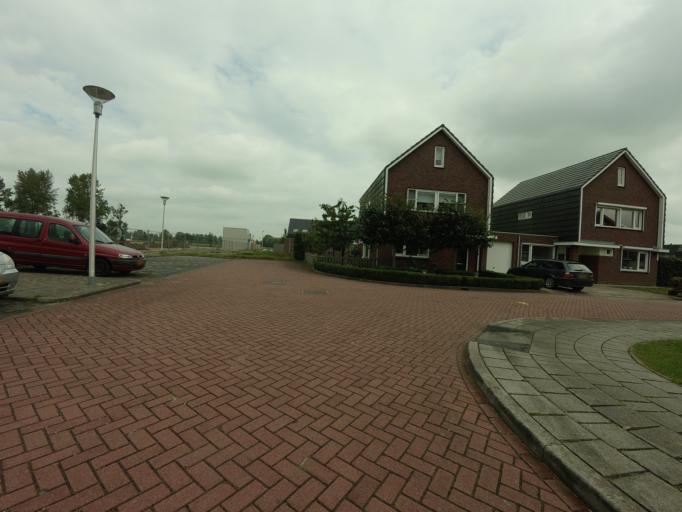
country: NL
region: Utrecht
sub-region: Gemeente Lopik
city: Lopik
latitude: 51.9068
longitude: 4.9404
